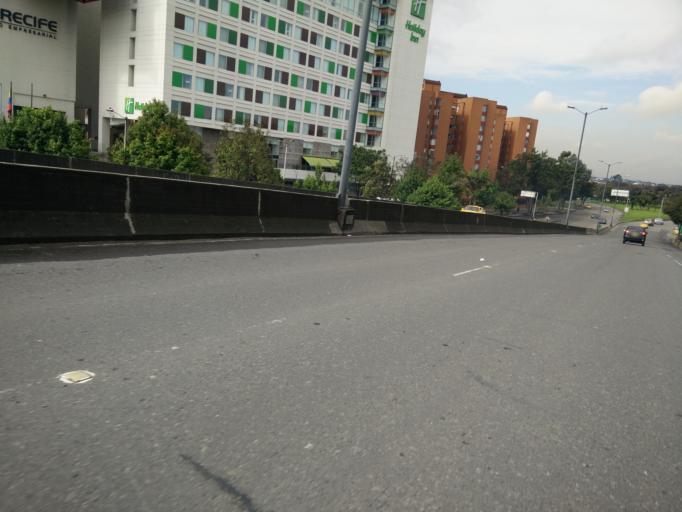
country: CO
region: Bogota D.C.
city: Bogota
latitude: 4.6628
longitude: -74.1099
